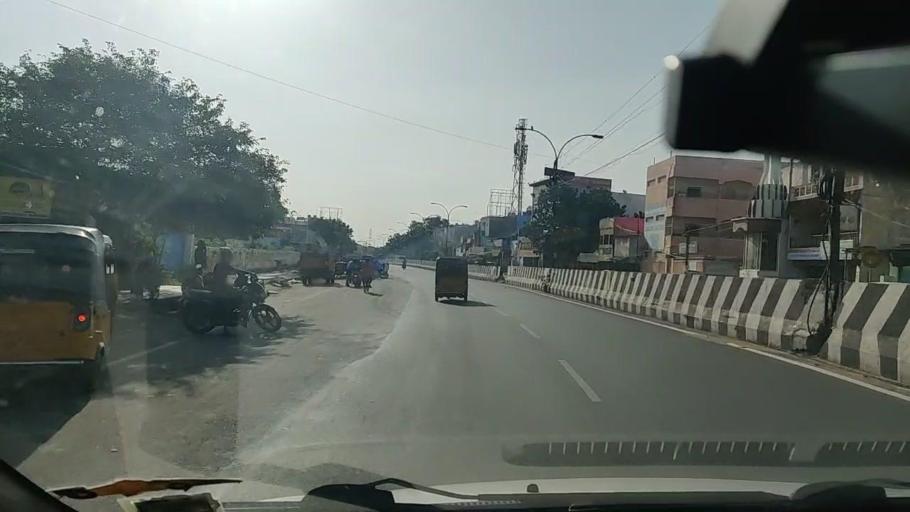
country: IN
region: Tamil Nadu
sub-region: Chennai
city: George Town
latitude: 13.1191
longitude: 80.2567
